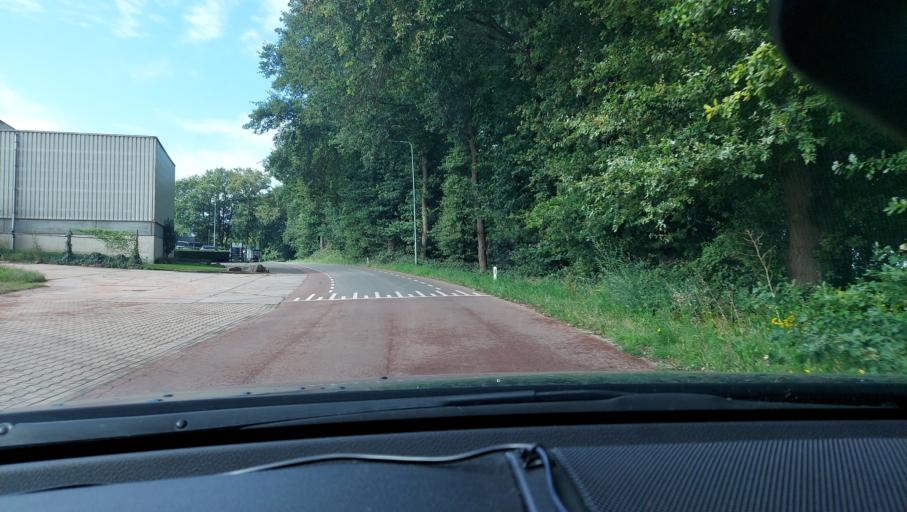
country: NL
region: Limburg
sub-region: Gemeente Beesel
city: Beesel
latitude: 51.2771
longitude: 6.0428
